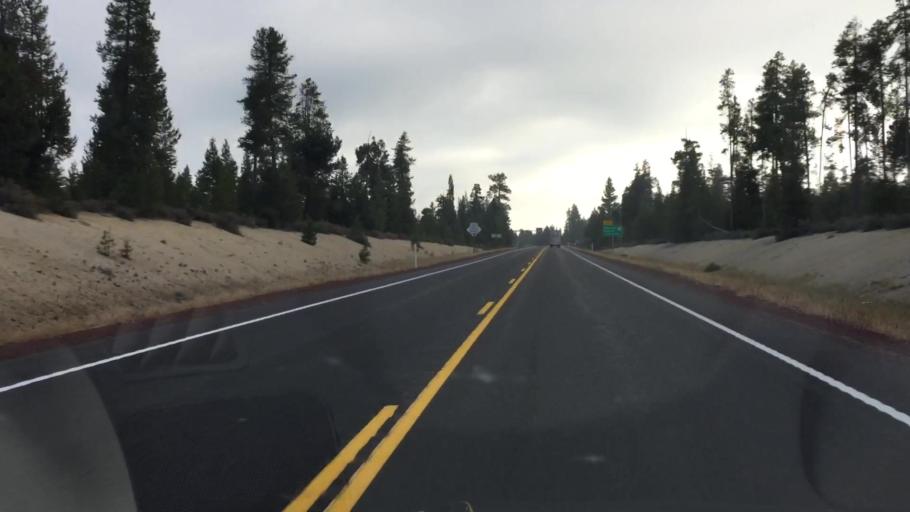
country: US
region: Oregon
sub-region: Deschutes County
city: La Pine
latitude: 43.3211
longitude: -121.7625
